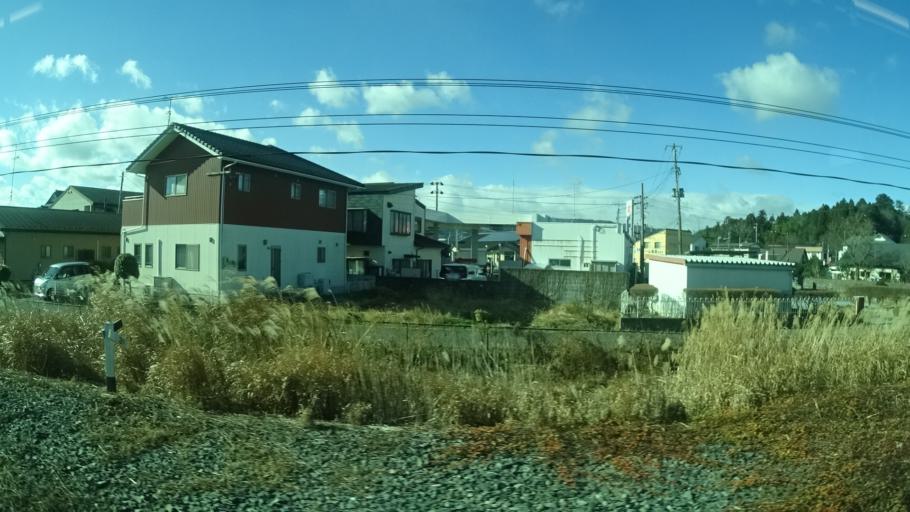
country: JP
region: Miyagi
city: Marumori
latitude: 37.8060
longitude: 140.9246
